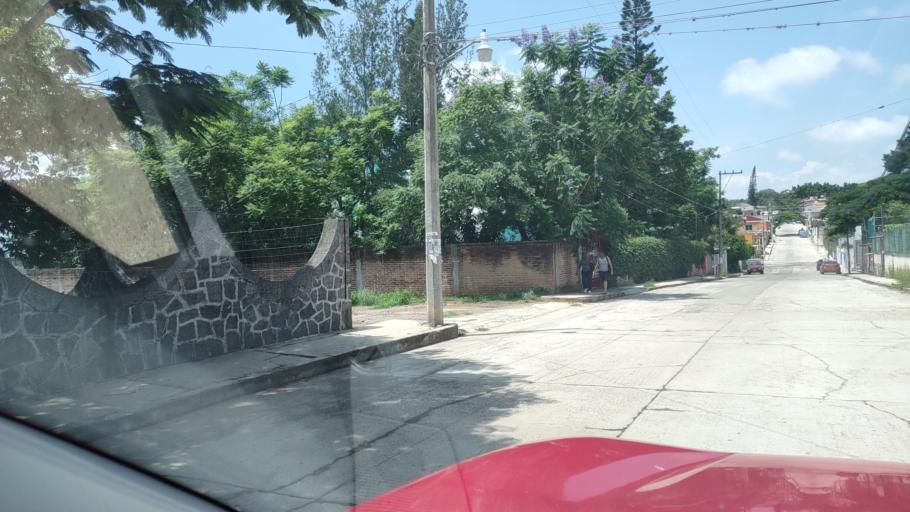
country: MX
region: Veracruz
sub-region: Emiliano Zapata
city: Dos Rios
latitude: 19.4892
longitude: -96.8141
